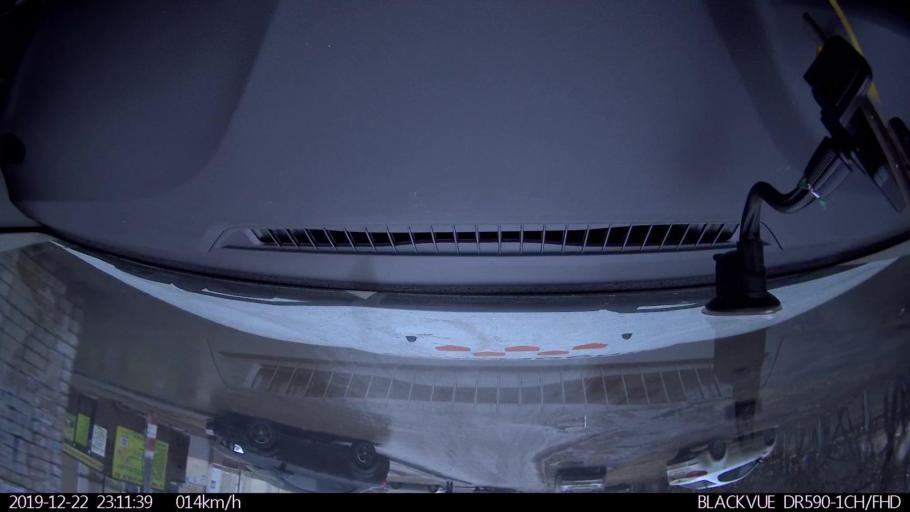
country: RU
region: Nizjnij Novgorod
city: Gorbatovka
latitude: 56.2612
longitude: 43.8495
